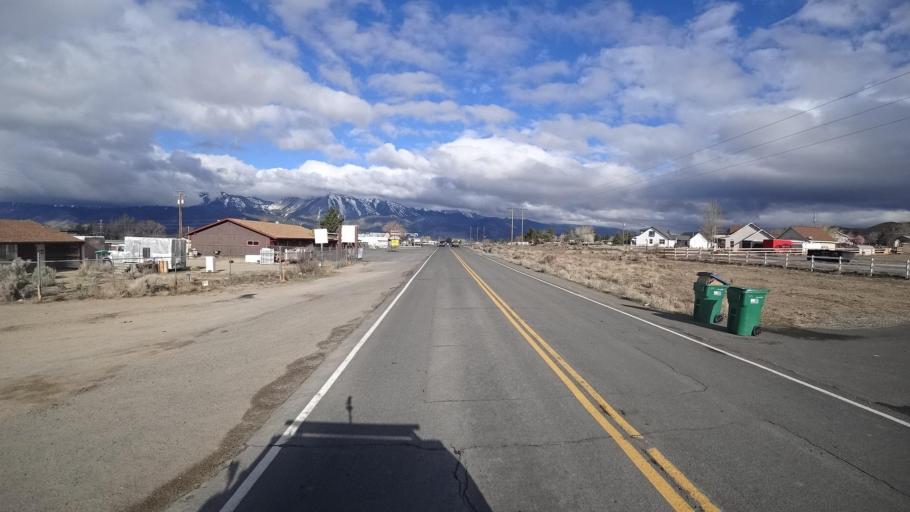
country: US
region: Nevada
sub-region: Storey County
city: Virginia City
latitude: 39.2904
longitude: -119.7680
